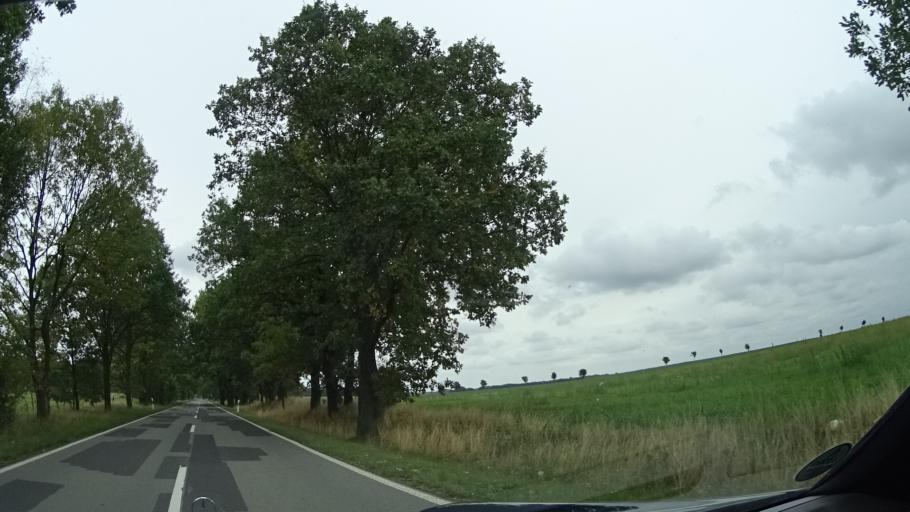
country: DE
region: Brandenburg
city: Walsleben
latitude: 52.9629
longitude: 12.7124
